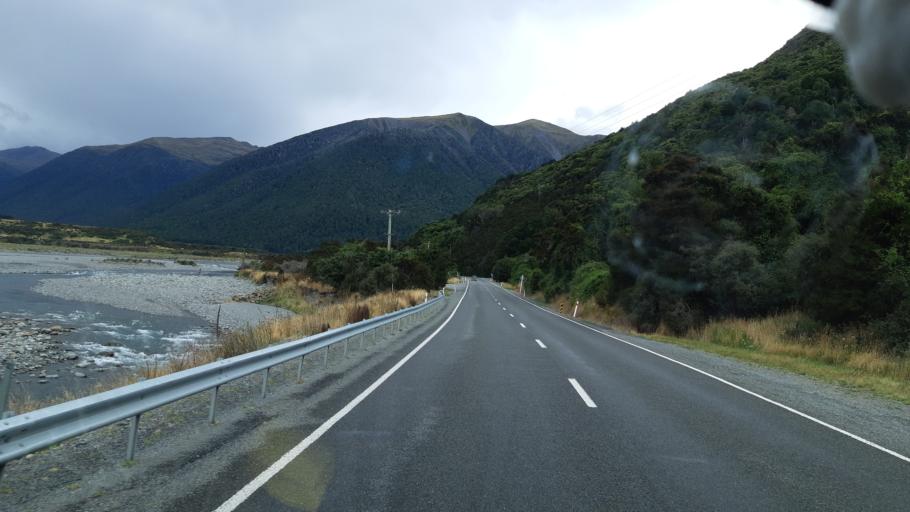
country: NZ
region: Canterbury
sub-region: Hurunui District
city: Amberley
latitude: -42.5599
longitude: 172.3516
